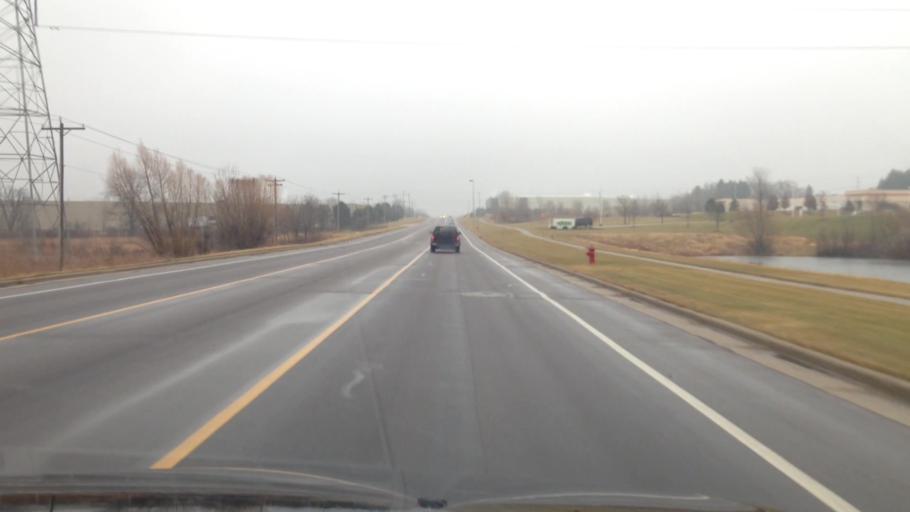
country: US
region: Wisconsin
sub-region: Washington County
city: Germantown
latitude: 43.2357
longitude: -88.1489
